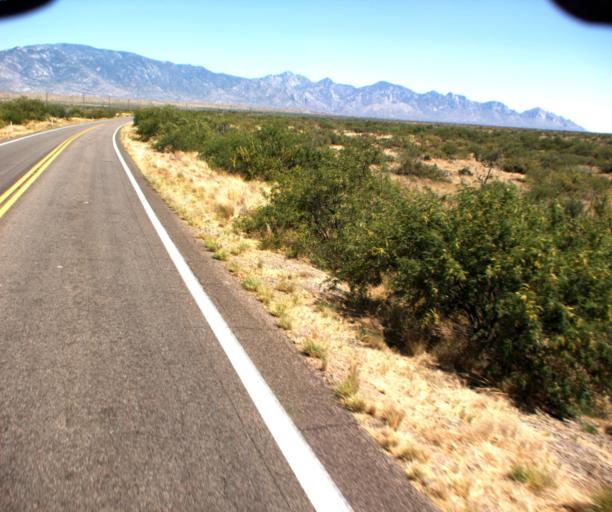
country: US
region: Arizona
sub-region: Pima County
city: Catalina
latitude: 32.5802
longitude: -110.9522
